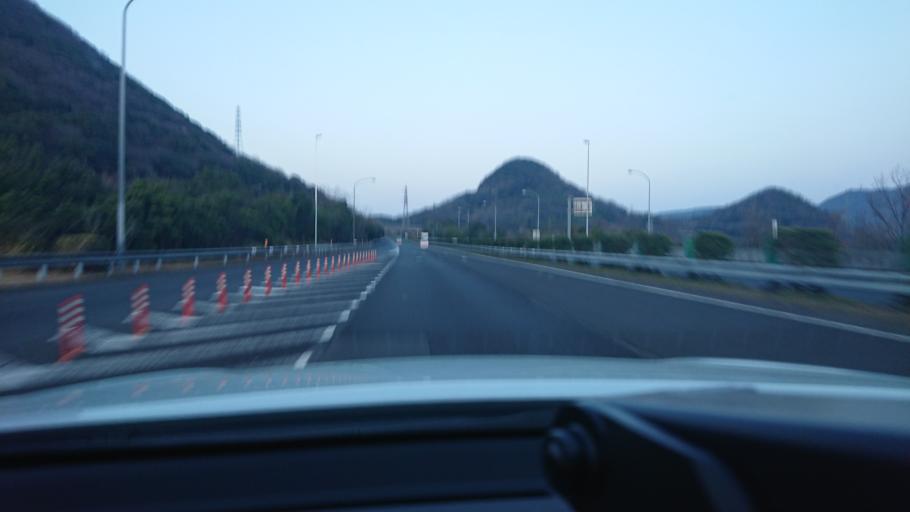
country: JP
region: Kagawa
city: Takamatsu-shi
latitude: 34.2953
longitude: 133.9858
